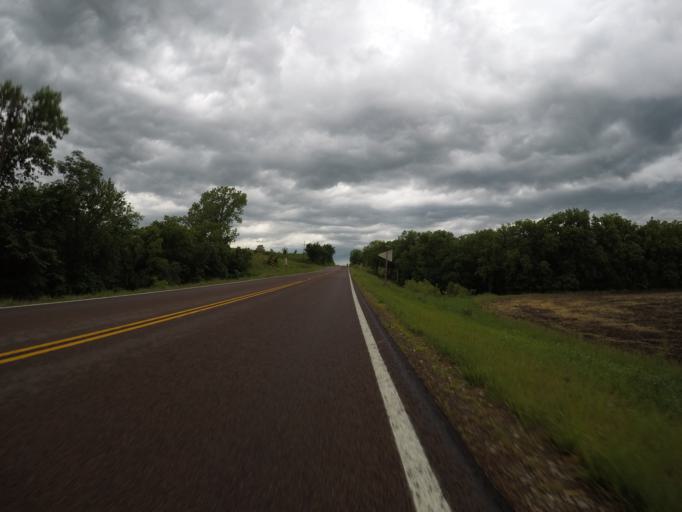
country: US
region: Kansas
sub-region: Shawnee County
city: Rossville
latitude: 38.9646
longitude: -95.9818
